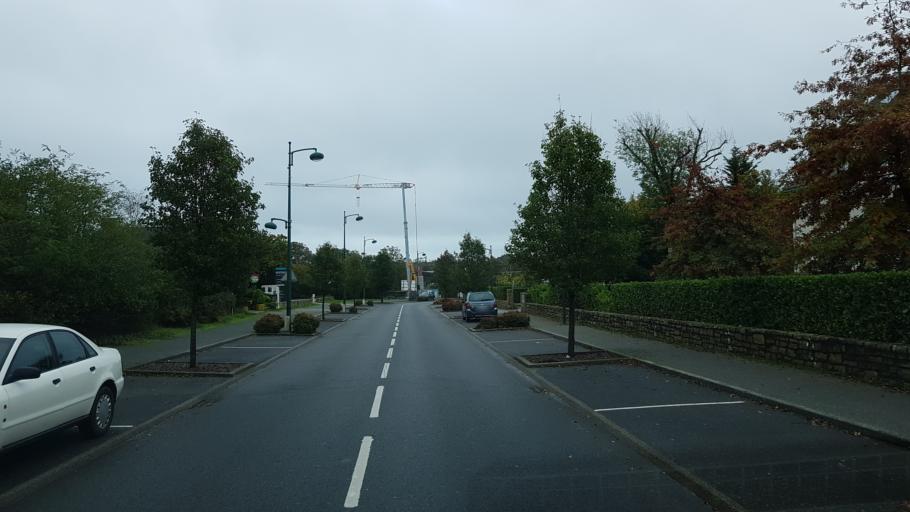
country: FR
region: Brittany
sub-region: Departement du Morbihan
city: Sarzeau
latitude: 47.5240
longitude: -2.7688
